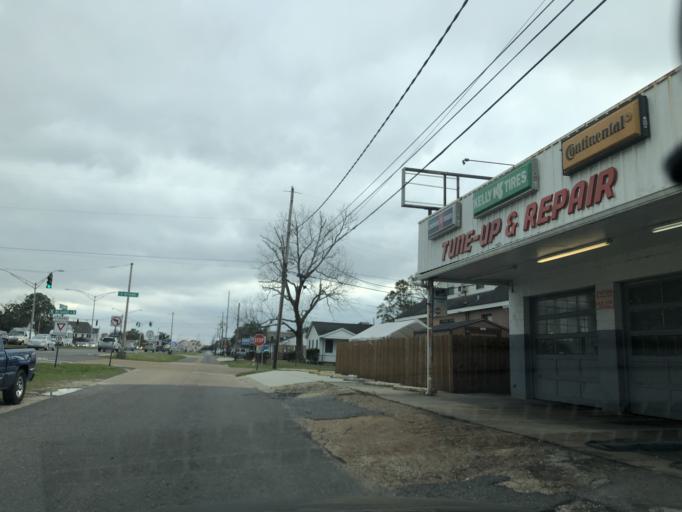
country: US
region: Louisiana
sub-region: Jefferson Parish
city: Metairie
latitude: 29.9825
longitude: -90.1563
